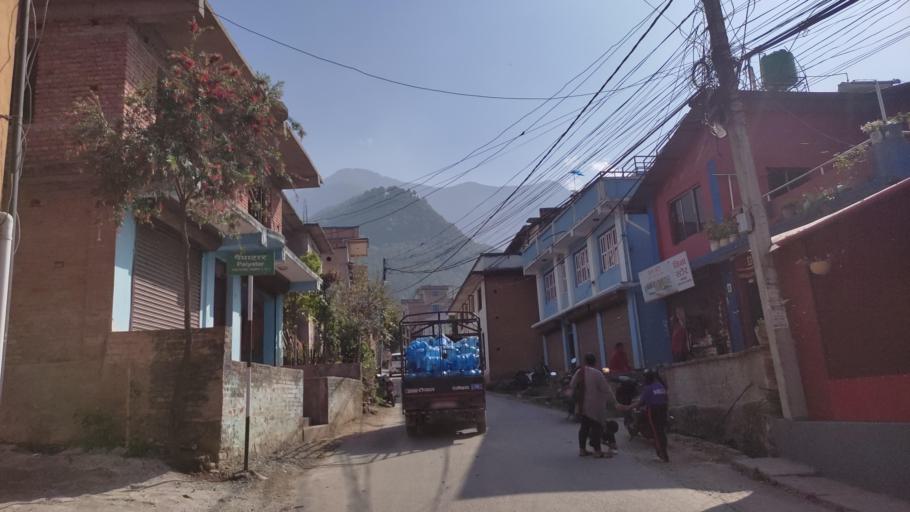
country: NP
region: Central Region
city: Kirtipur
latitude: 27.6720
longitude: 85.2510
